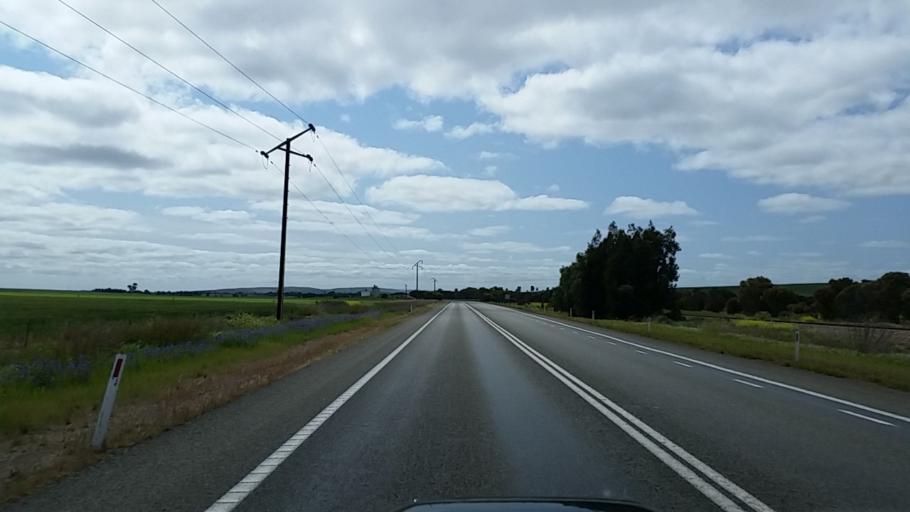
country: AU
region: South Australia
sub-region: Port Pirie City and Dists
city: Crystal Brook
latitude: -33.5674
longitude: 138.2247
